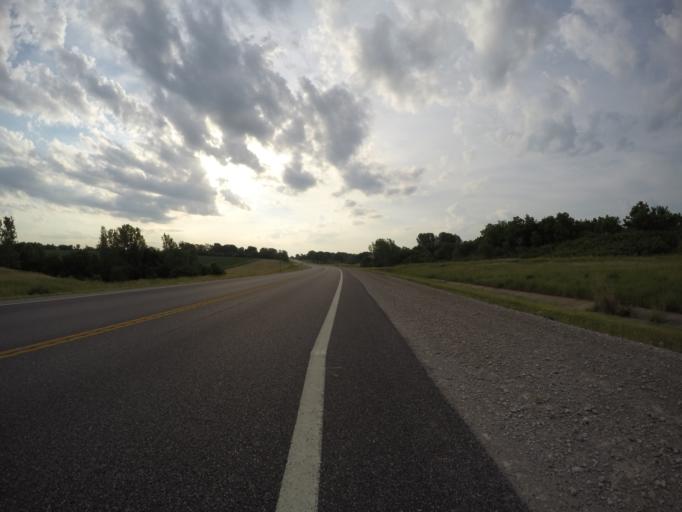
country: US
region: Kansas
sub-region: Doniphan County
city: Troy
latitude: 39.7926
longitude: -95.0744
